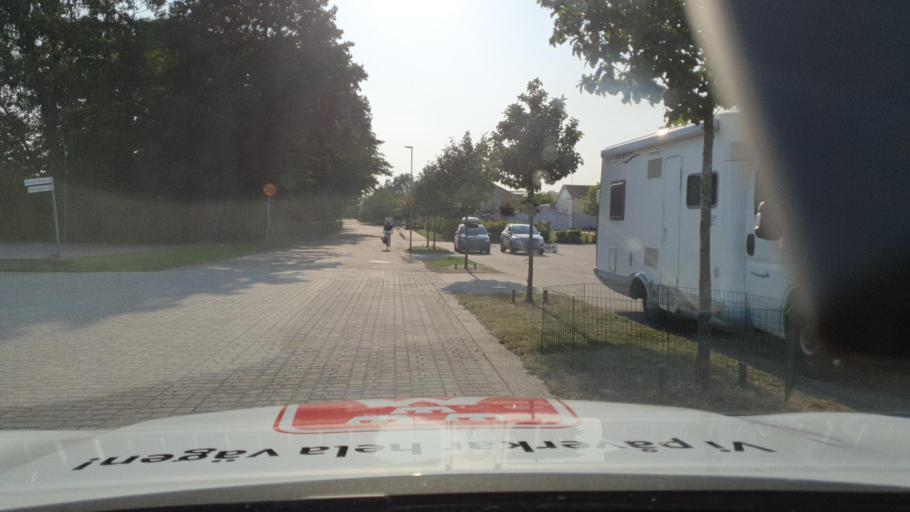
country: SE
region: Skane
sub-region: Hoganas Kommun
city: Hoganas
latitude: 56.2289
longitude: 12.6784
